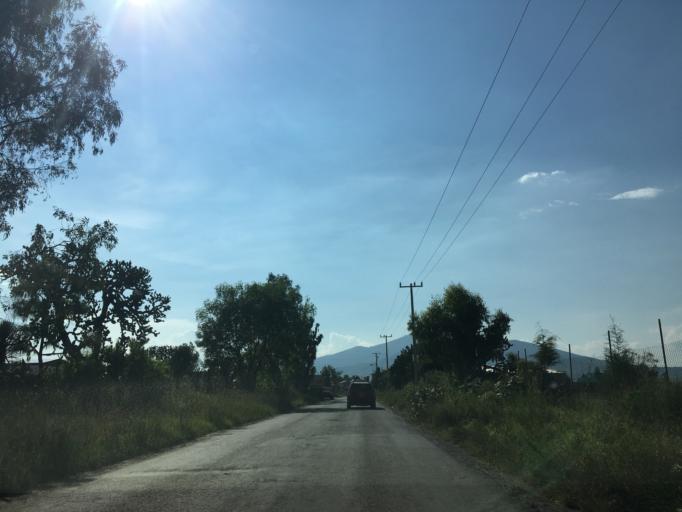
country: MX
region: Michoacan
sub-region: Morelia
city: La Mintzita (Piedra Dura)
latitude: 19.5948
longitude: -101.2750
